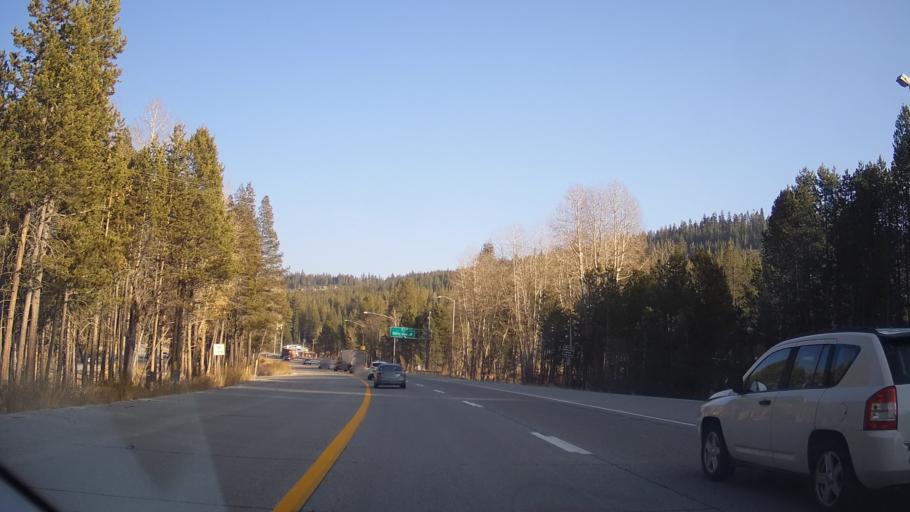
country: US
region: California
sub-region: Nevada County
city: Truckee
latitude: 39.3138
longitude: -120.4509
